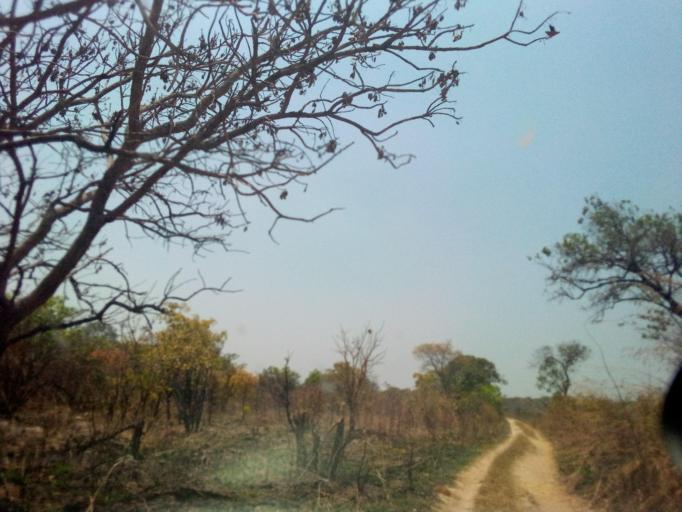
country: ZM
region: Copperbelt
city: Kataba
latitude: -12.2483
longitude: 30.3935
